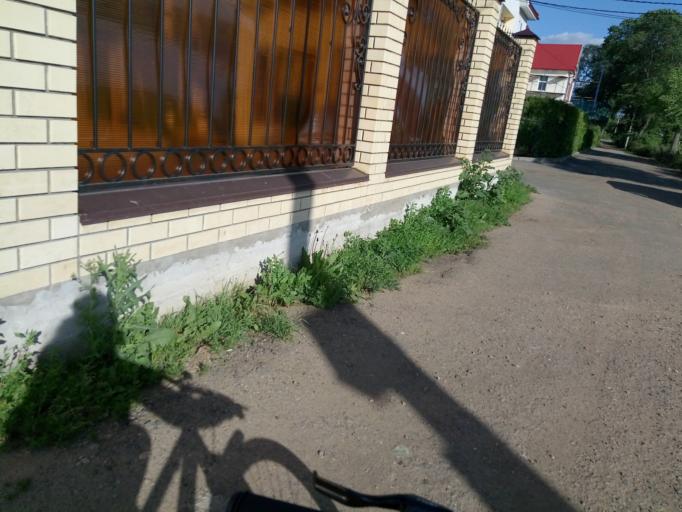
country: RU
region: Jaroslavl
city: Yaroslavl
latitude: 57.6341
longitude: 39.9055
